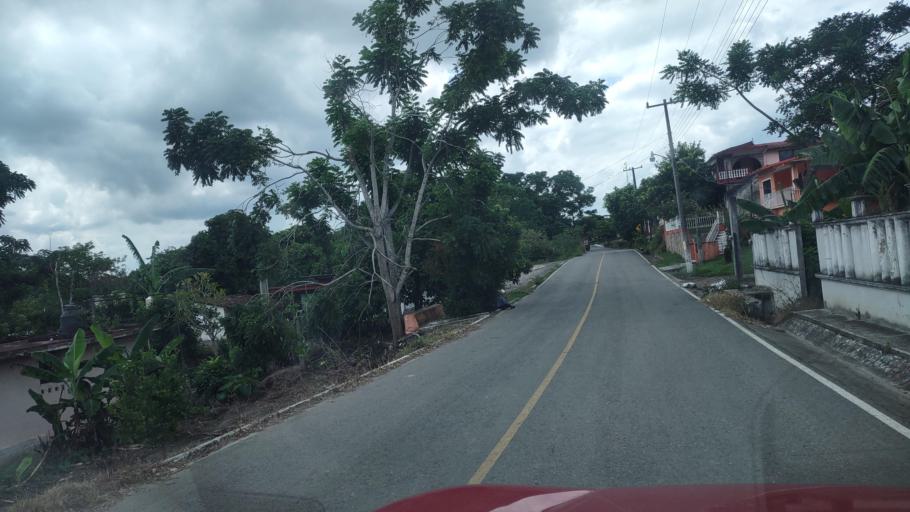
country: MX
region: Puebla
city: San Jose Acateno
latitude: 20.2232
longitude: -97.1350
